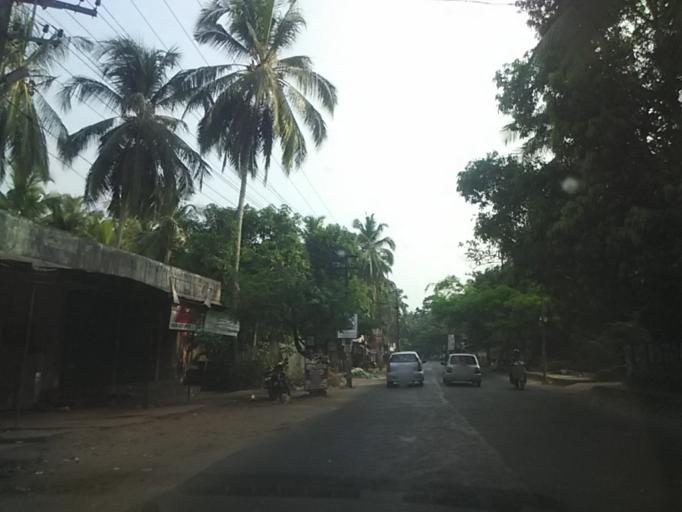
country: IN
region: Kerala
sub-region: Kozhikode
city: Kozhikode
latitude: 11.3476
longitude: 75.7618
